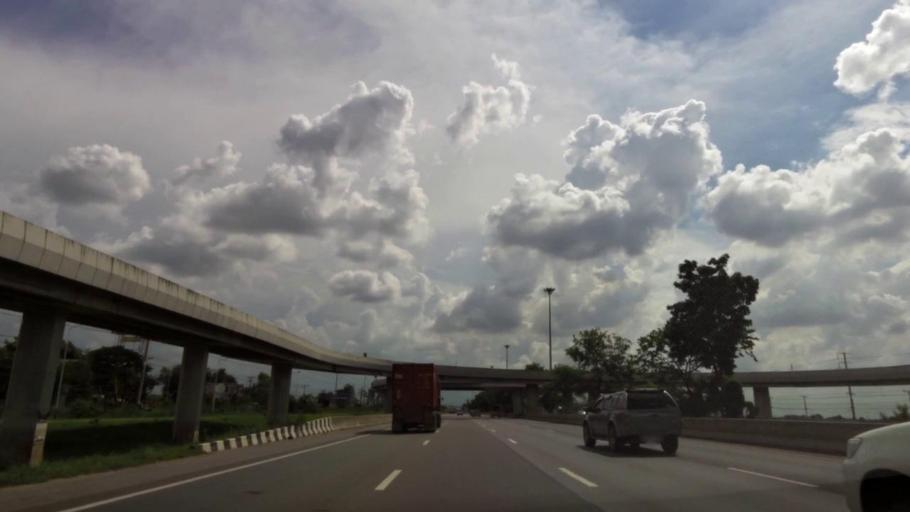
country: TH
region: Phra Nakhon Si Ayutthaya
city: Bang Pa-in
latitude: 14.2769
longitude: 100.6135
